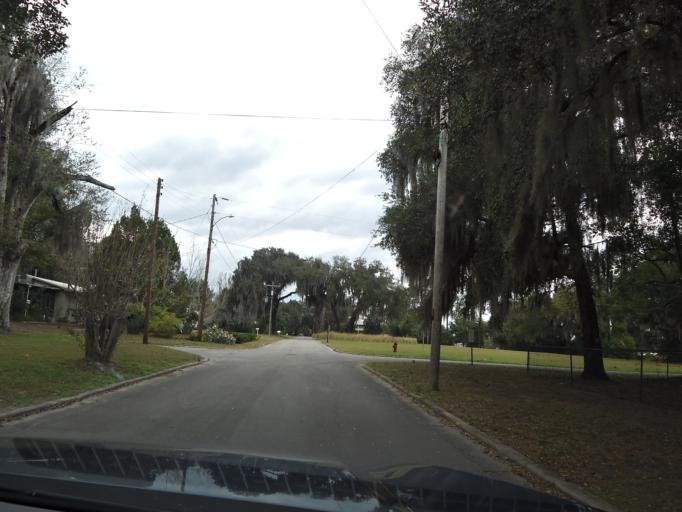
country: US
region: Florida
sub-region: Putnam County
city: Crescent City
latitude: 29.4337
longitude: -81.5071
